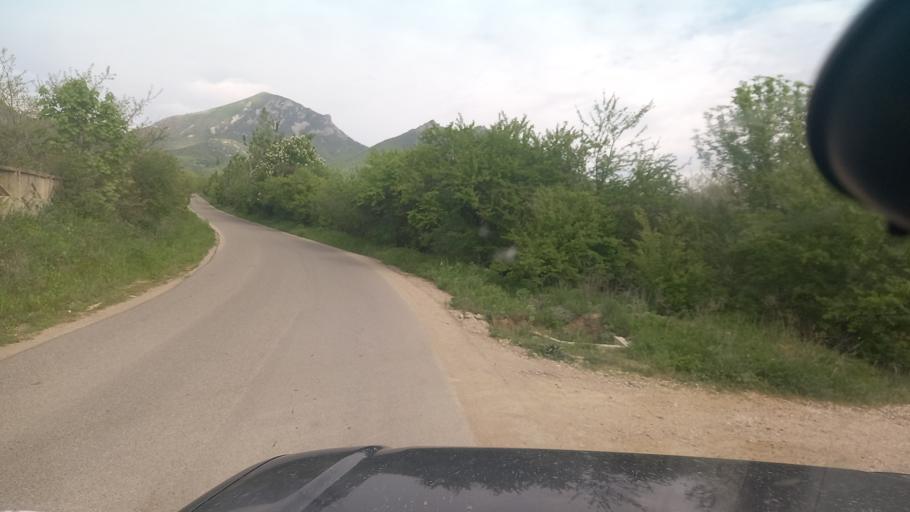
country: RU
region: Stavropol'skiy
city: Pyatigorsk
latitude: 44.0702
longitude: 43.0523
